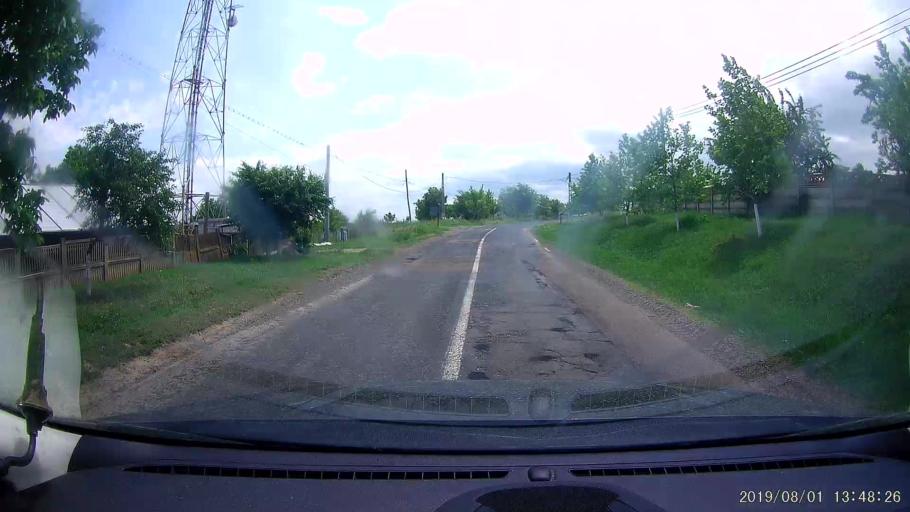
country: RO
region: Galati
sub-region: Comuna Oancea
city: Oancea
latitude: 45.9081
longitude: 28.1120
